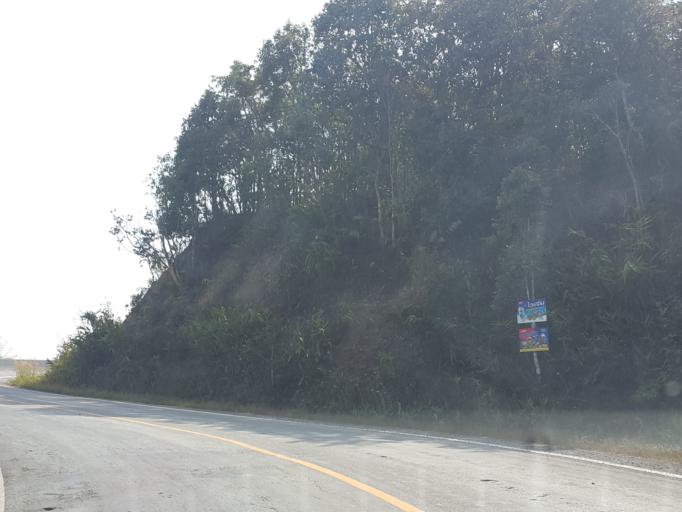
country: TH
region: Chiang Mai
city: Hot
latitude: 18.0820
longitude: 98.3668
